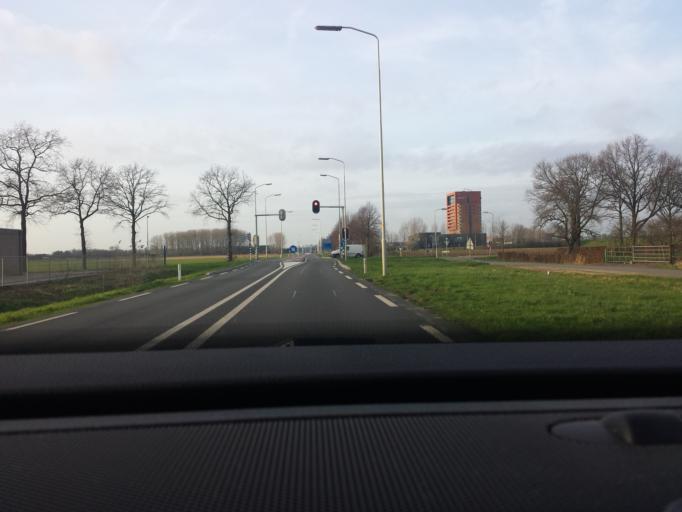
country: NL
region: Gelderland
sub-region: Gemeente Duiven
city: Duiven
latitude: 51.9558
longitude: 6.0287
